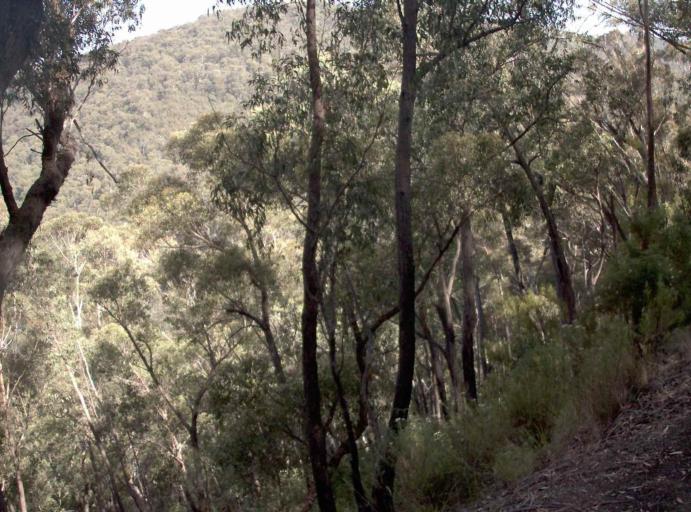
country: AU
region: Victoria
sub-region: East Gippsland
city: Lakes Entrance
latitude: -37.3973
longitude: 148.1226
